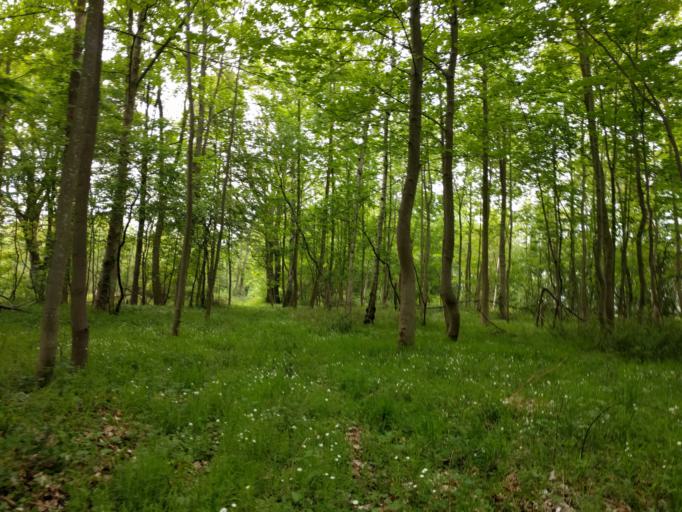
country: DK
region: South Denmark
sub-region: Kerteminde Kommune
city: Munkebo
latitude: 55.4176
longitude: 10.5434
